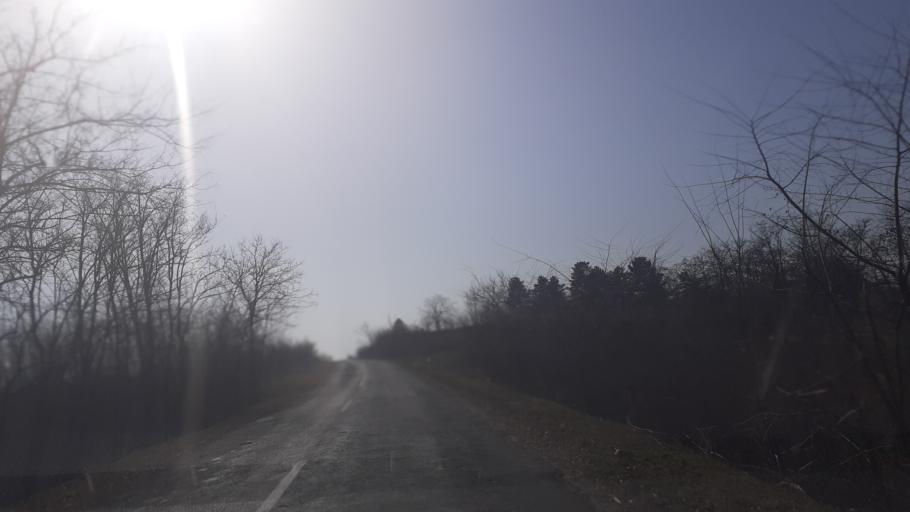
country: HU
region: Pest
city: Dabas
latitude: 47.1484
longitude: 19.3294
